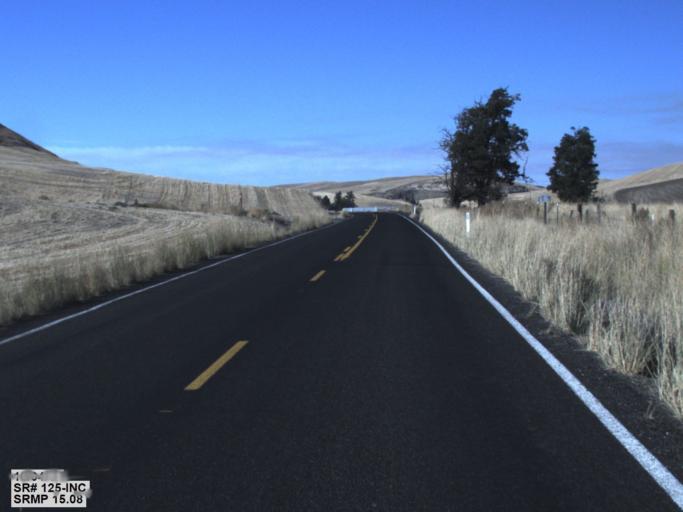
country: US
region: Washington
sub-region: Walla Walla County
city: Walla Walla
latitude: 46.1870
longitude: -118.3836
